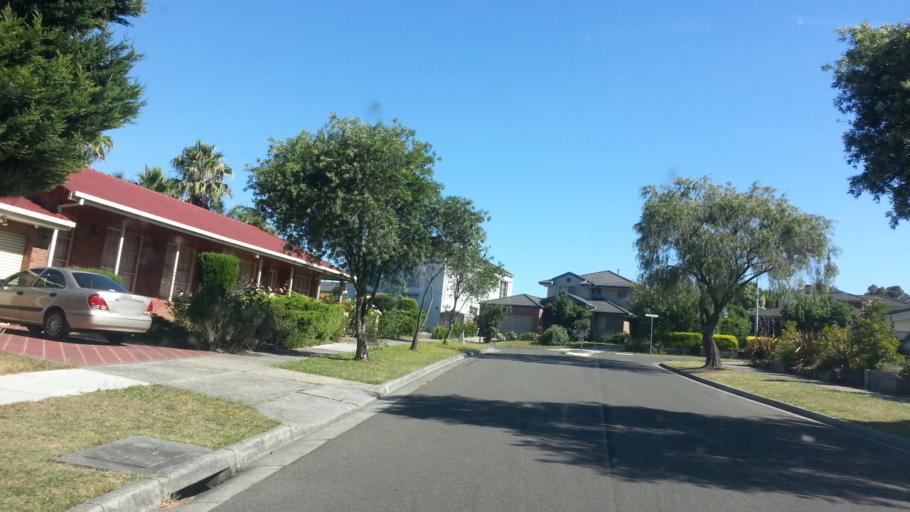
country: AU
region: Victoria
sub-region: Knox
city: Rowville
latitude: -37.9244
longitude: 145.2599
